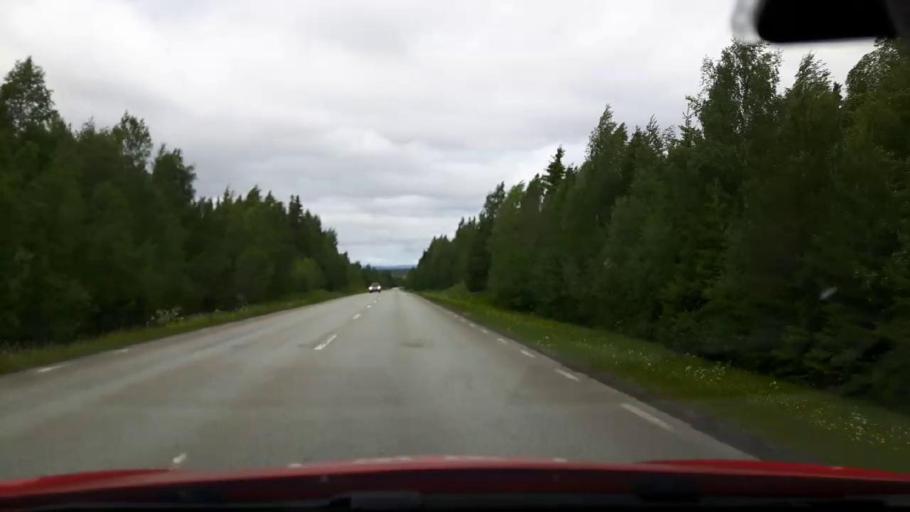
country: SE
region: Jaemtland
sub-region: Krokoms Kommun
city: Krokom
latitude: 63.3926
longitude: 14.5028
